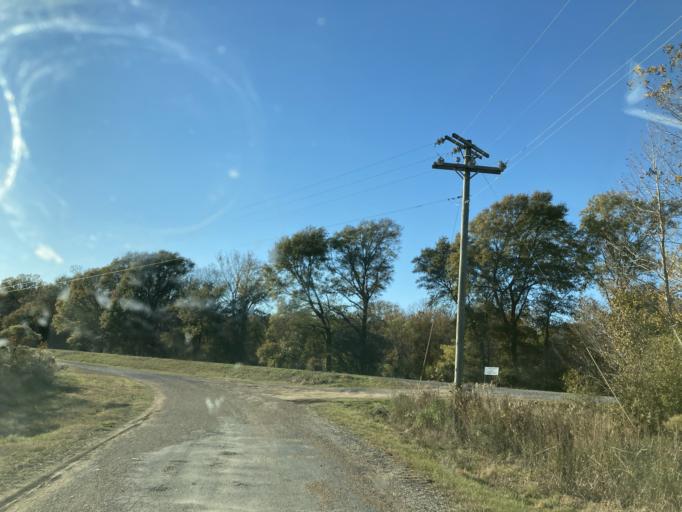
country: US
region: Mississippi
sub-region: Yazoo County
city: Yazoo City
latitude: 32.9899
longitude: -90.3551
